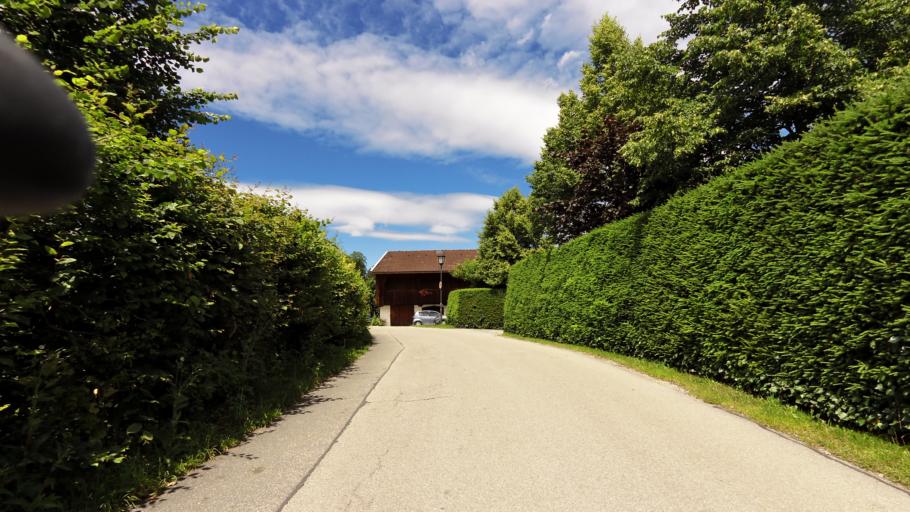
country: DE
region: Bavaria
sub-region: Upper Bavaria
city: Tegernsee
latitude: 47.7025
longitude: 11.7379
